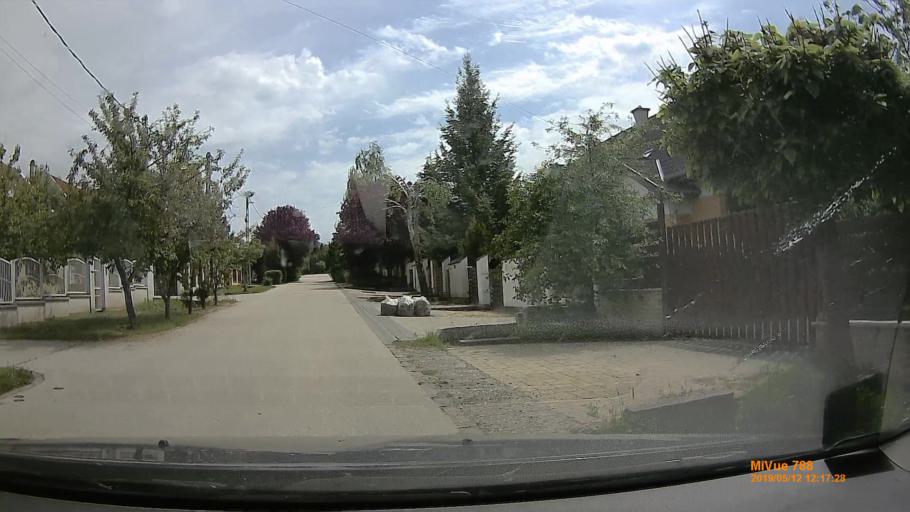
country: HU
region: Budapest
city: Budapest XVII. keruelet
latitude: 47.4672
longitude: 19.2890
